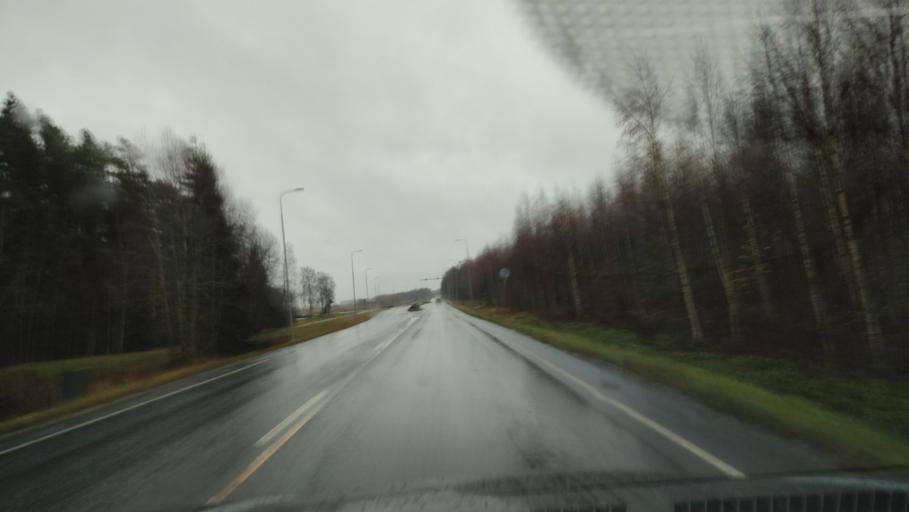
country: FI
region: Ostrobothnia
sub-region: Vaasa
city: Ristinummi
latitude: 63.0501
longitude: 21.7263
